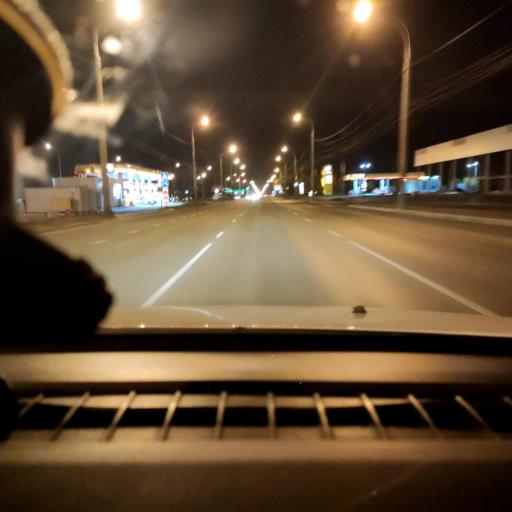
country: RU
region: Samara
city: Samara
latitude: 53.1411
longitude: 50.1793
